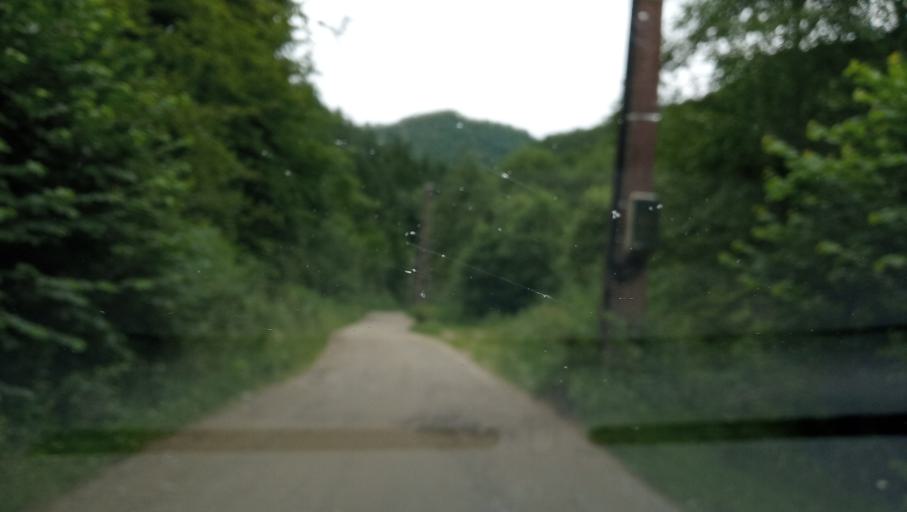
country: RO
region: Hunedoara
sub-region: Oras Petrila
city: Petrila
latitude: 45.4816
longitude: 23.4167
